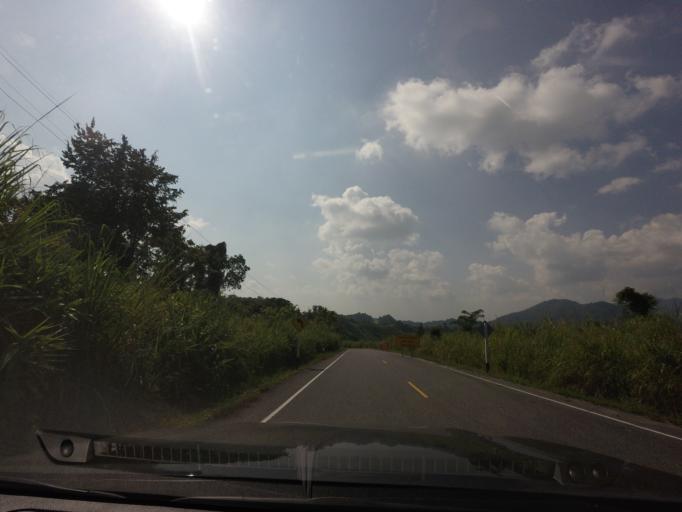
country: TH
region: Nan
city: Santi Suk
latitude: 18.9727
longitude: 101.0255
